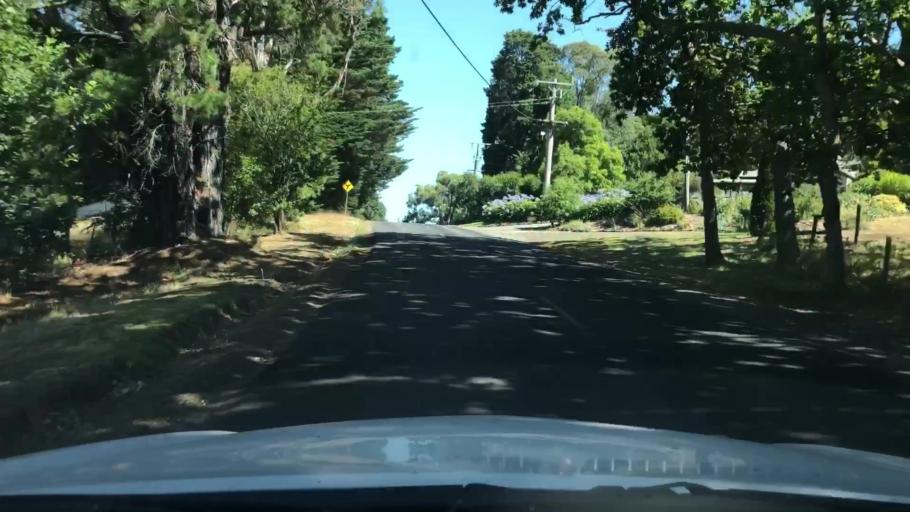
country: AU
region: Victoria
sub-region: Yarra Ranges
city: Macclesfield
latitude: -37.8840
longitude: 145.4767
